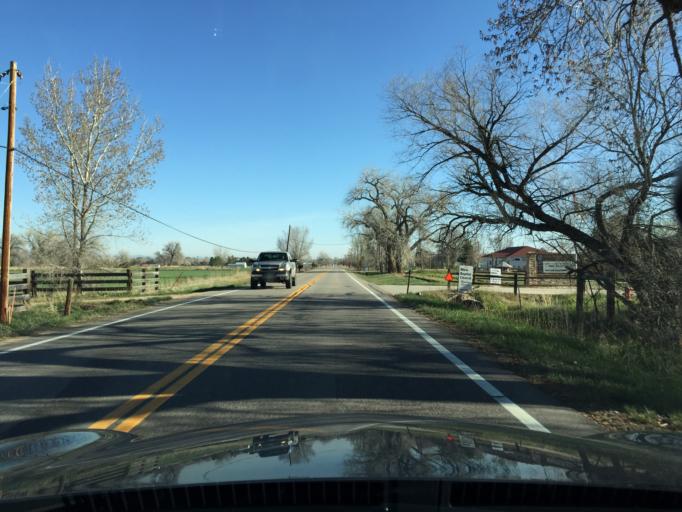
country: US
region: Colorado
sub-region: Boulder County
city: Erie
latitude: 40.0728
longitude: -105.0554
